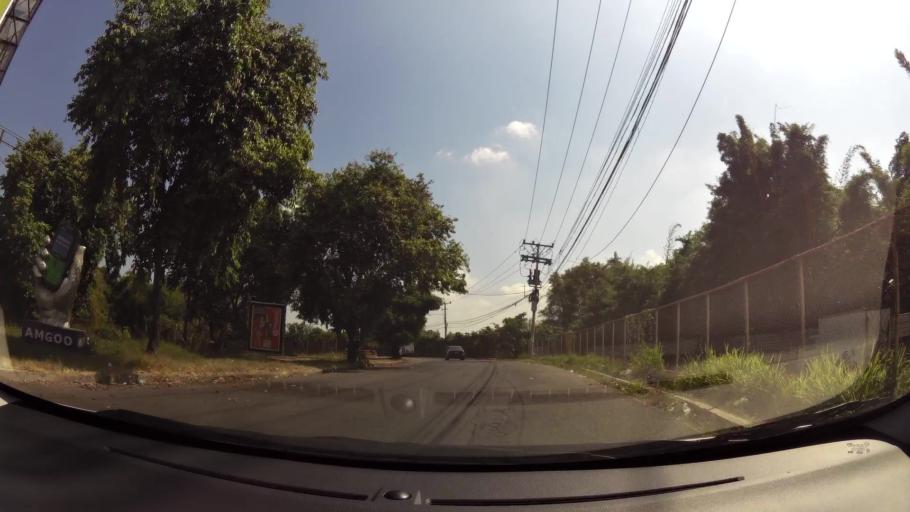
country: SV
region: La Libertad
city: Antiguo Cuscatlan
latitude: 13.6690
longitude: -89.2650
